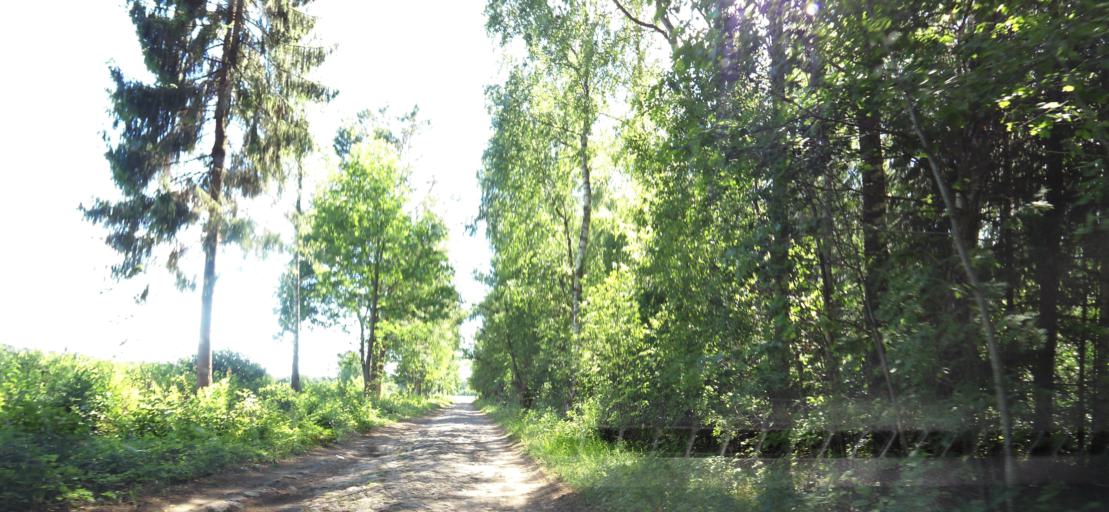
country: LT
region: Vilnius County
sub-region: Vilnius
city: Fabijoniskes
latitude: 54.8383
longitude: 25.3257
